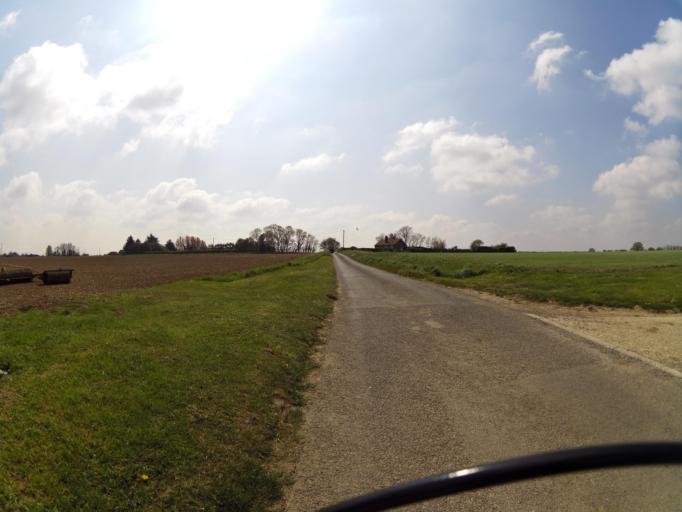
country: GB
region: England
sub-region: Suffolk
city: Bramford
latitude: 52.0767
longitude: 1.0261
